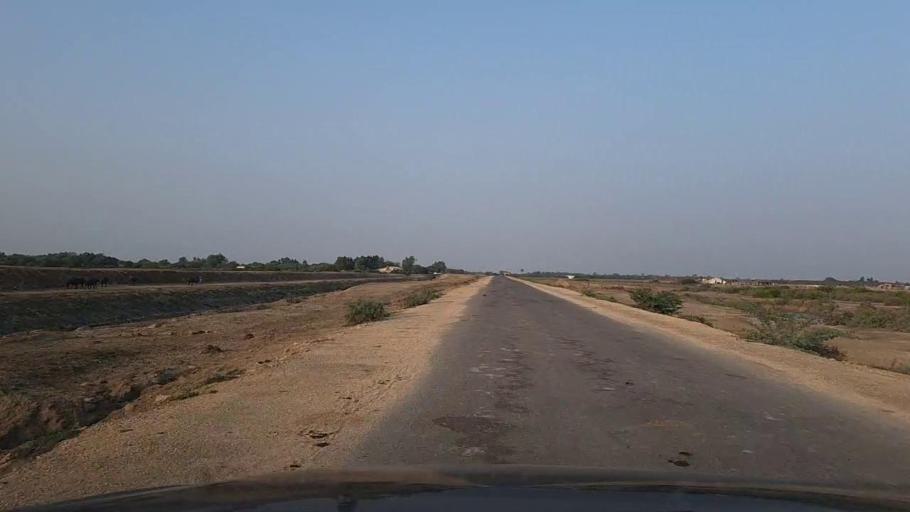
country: PK
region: Sindh
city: Mirpur Sakro
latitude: 24.4835
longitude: 67.8062
